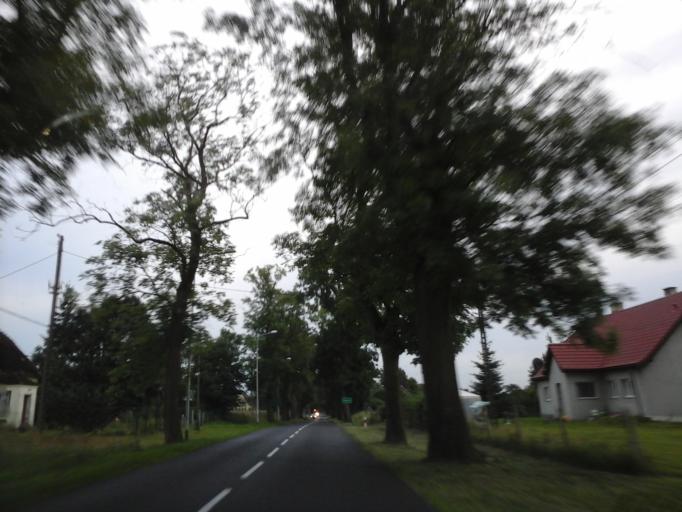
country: PL
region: West Pomeranian Voivodeship
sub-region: Powiat goleniowski
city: Maszewo
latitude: 53.5489
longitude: 15.1253
